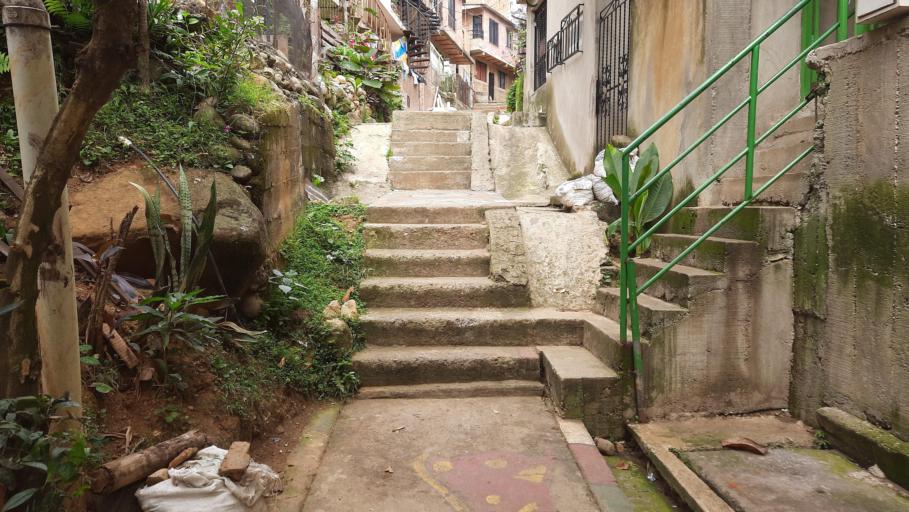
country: CO
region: Valle del Cauca
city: Cali
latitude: 3.3744
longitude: -76.5564
